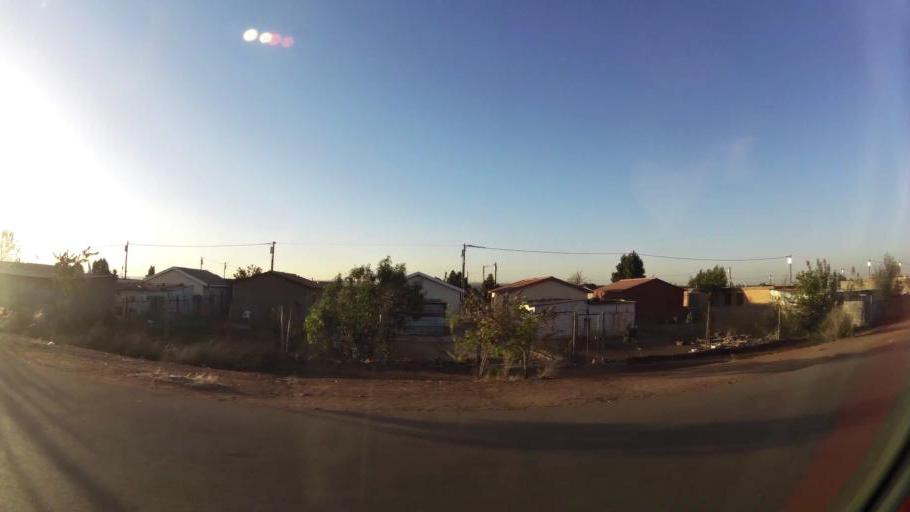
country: ZA
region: North-West
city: Ga-Rankuwa
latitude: -25.5975
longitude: 28.0874
